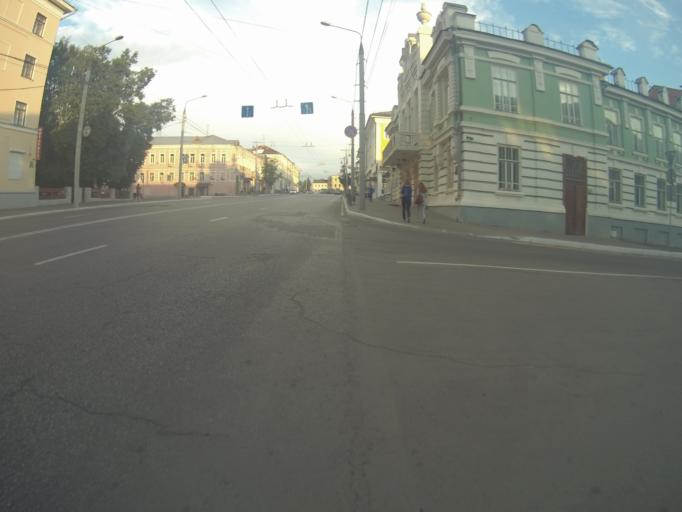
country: RU
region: Vladimir
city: Vladimir
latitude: 56.1304
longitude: 40.4034
